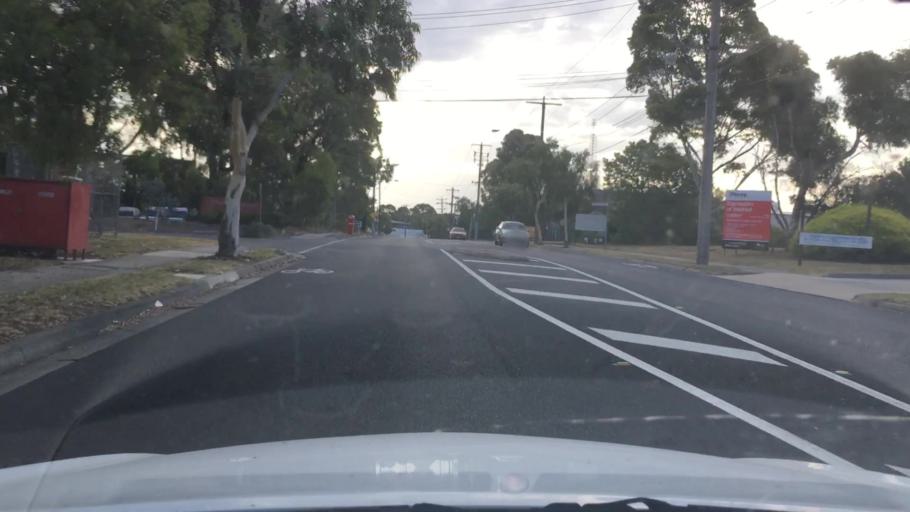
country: AU
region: Victoria
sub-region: Greater Dandenong
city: Noble Park North
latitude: -37.9503
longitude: 145.1854
